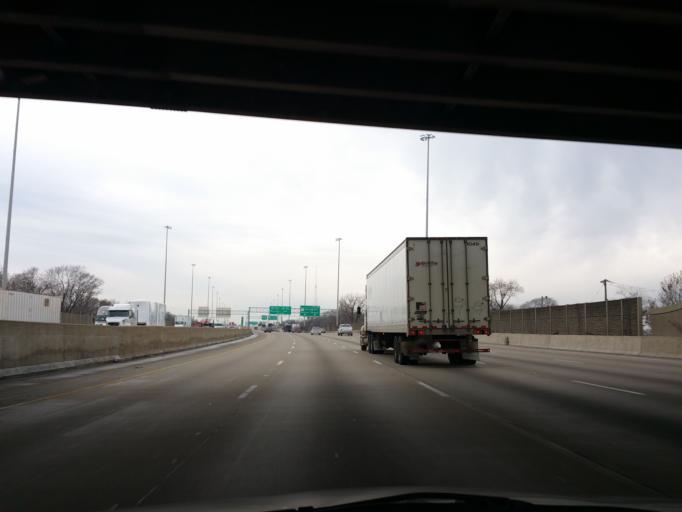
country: US
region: Illinois
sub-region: Cook County
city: Lansing
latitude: 41.5778
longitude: -87.5299
